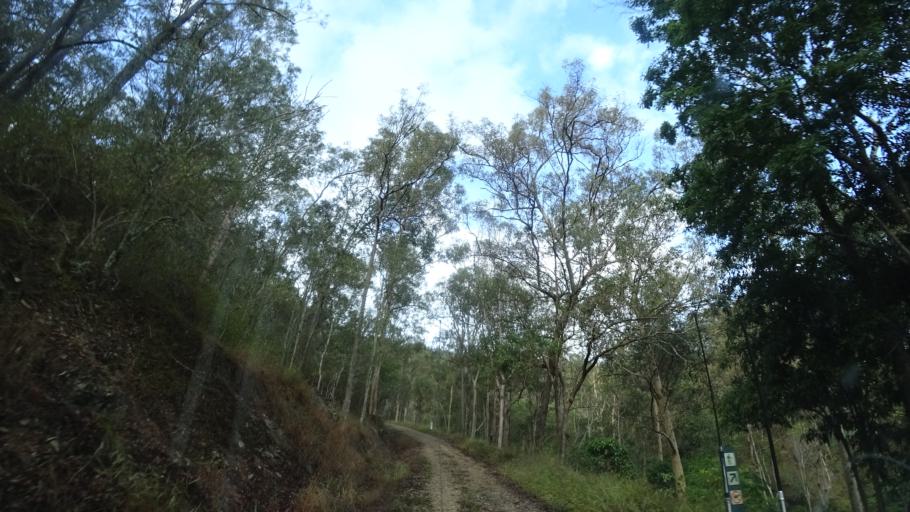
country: AU
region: Queensland
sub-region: Brisbane
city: Pullenvale
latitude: -27.4620
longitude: 152.8805
